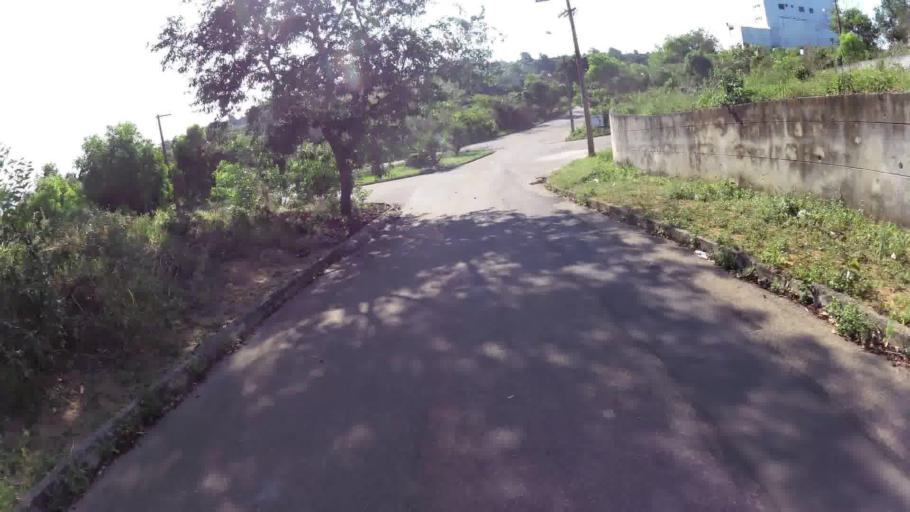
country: BR
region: Espirito Santo
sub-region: Guarapari
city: Guarapari
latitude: -20.7217
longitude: -40.5278
